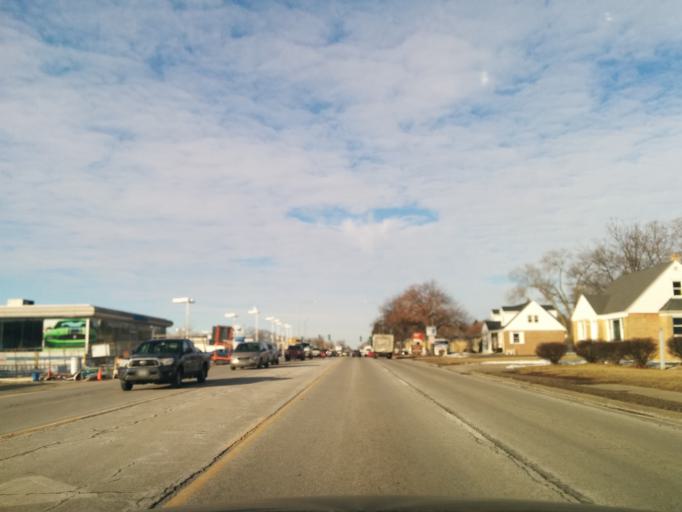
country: US
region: Illinois
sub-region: DuPage County
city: Glen Ellyn
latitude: 41.8592
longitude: -88.0798
